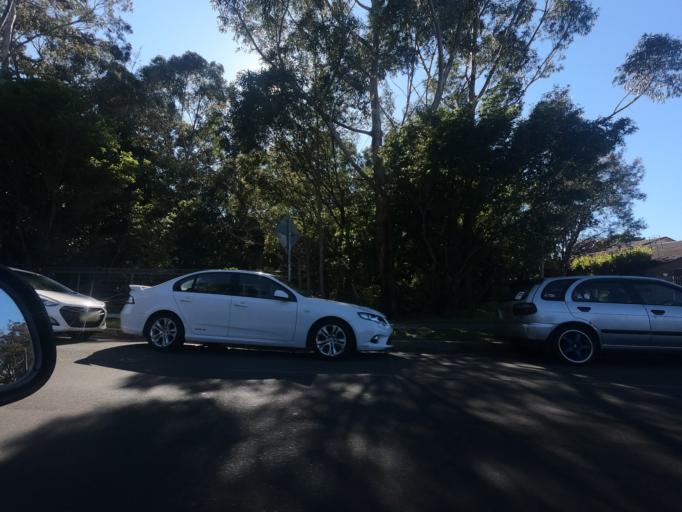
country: AU
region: New South Wales
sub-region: Wollongong
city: Corrimal
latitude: -34.3809
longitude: 150.8880
